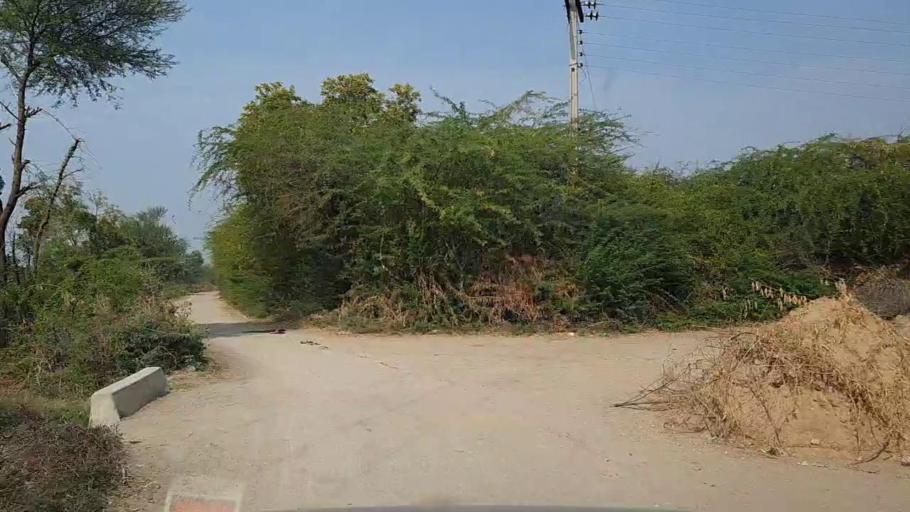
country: PK
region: Sindh
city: Mirwah Gorchani
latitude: 25.3422
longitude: 69.0636
